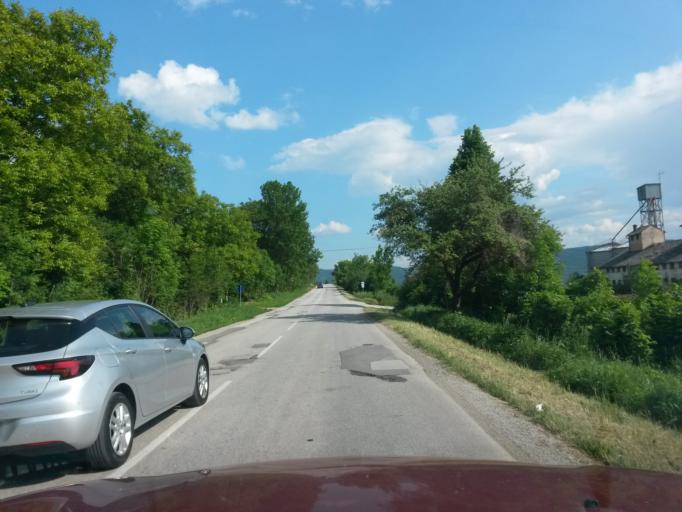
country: SK
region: Kosicky
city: Roznava
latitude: 48.6554
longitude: 20.5510
